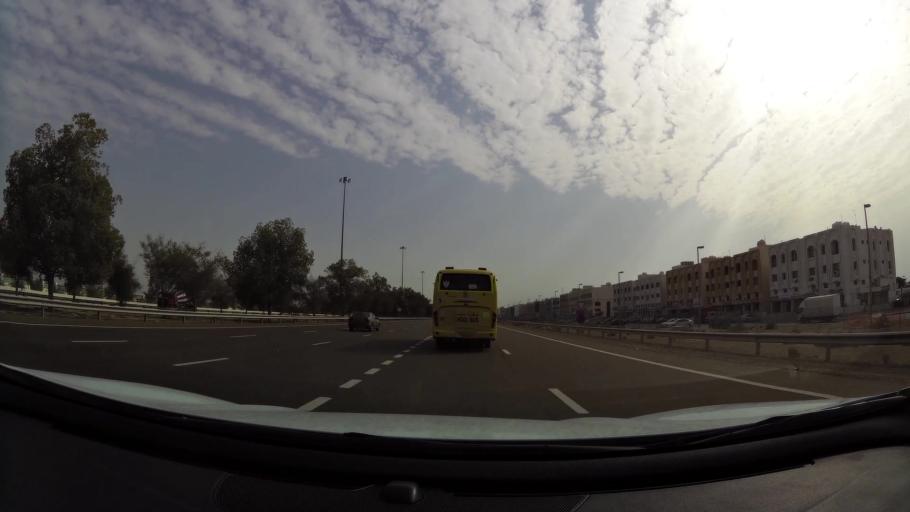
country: AE
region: Abu Dhabi
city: Abu Dhabi
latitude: 24.5387
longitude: 54.6930
